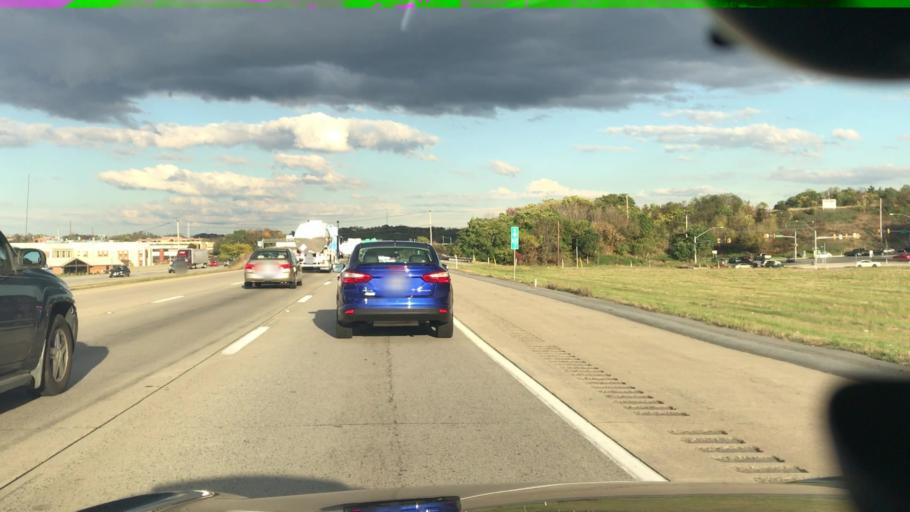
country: US
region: Pennsylvania
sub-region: Dauphin County
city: Progress
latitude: 40.3029
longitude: -76.8518
